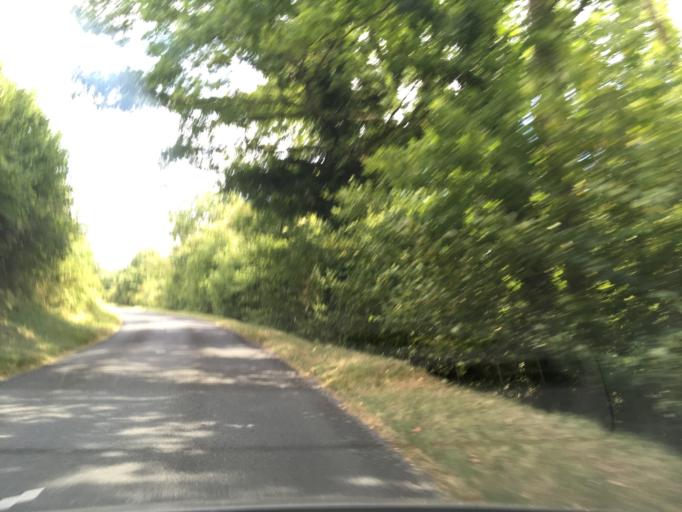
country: FR
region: Haute-Normandie
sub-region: Departement de l'Eure
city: Heudreville-sur-Eure
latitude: 49.1322
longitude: 1.2203
